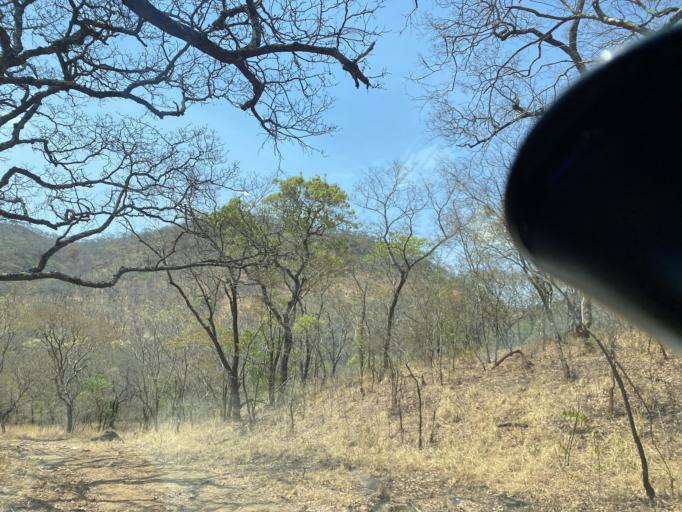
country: ZM
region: Lusaka
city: Kafue
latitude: -15.7436
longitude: 28.4724
